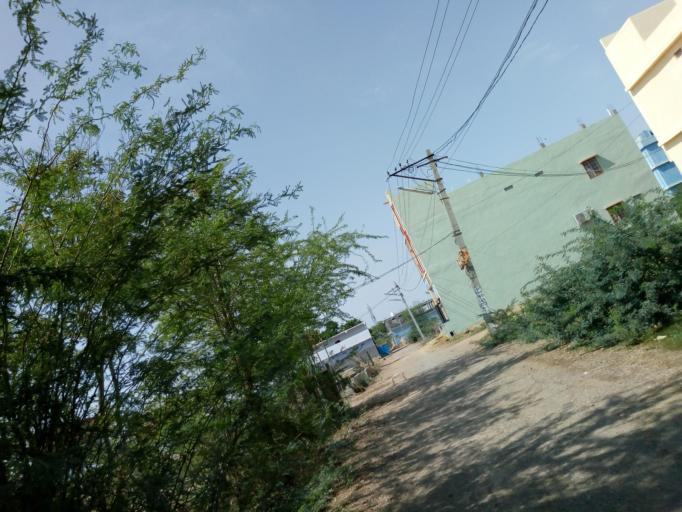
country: IN
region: Andhra Pradesh
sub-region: Prakasam
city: Cumbum
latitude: 15.5855
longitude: 79.1109
